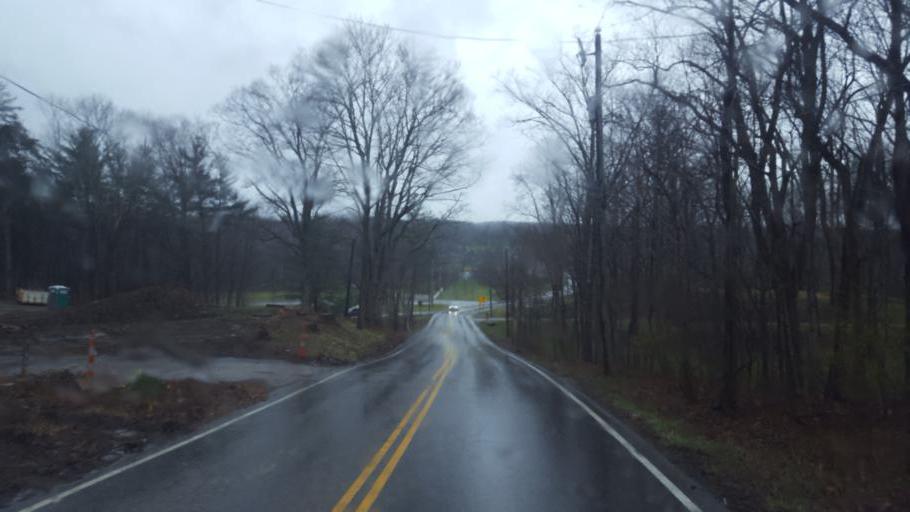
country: US
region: Ohio
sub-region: Delaware County
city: Powell
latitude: 40.1757
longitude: -83.0415
